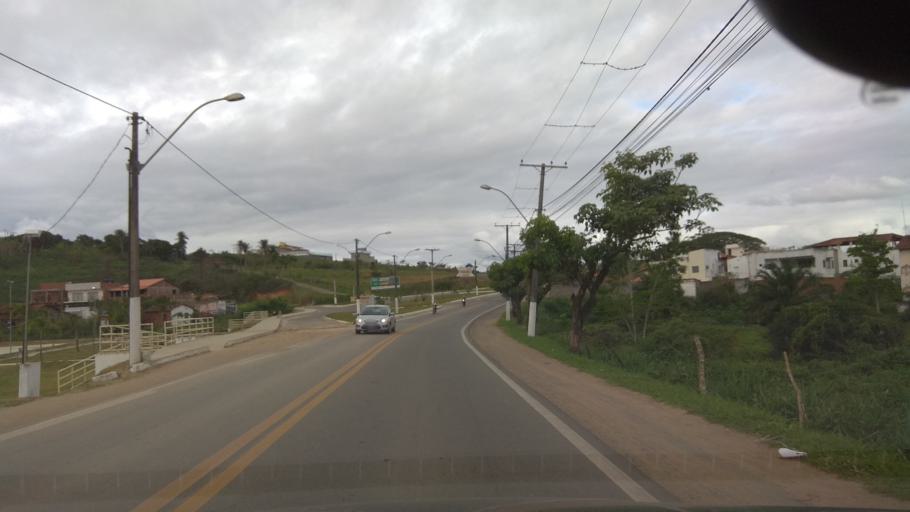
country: BR
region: Bahia
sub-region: Ipiau
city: Ipiau
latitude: -14.1390
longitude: -39.7318
